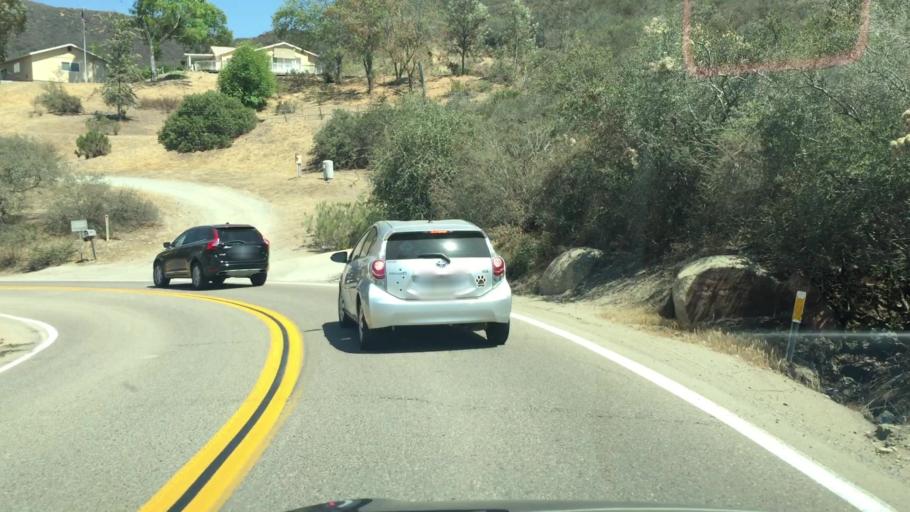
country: US
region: California
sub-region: San Diego County
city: Jamul
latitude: 32.7352
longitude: -116.8169
